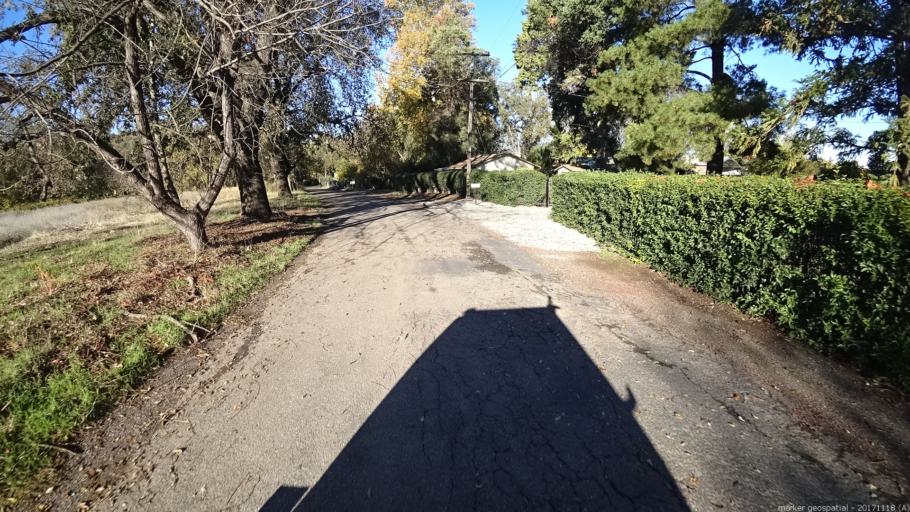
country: US
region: California
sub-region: Shasta County
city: Anderson
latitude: 40.4608
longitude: -122.2353
